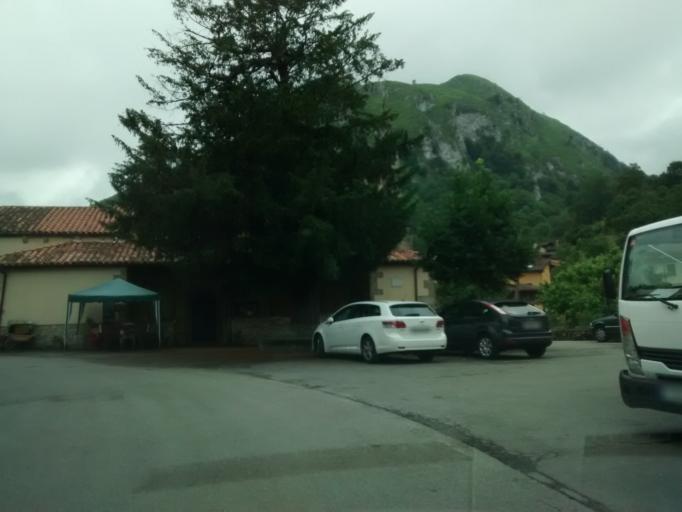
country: ES
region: Asturias
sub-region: Province of Asturias
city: Pilona
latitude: 43.3001
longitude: -5.3629
